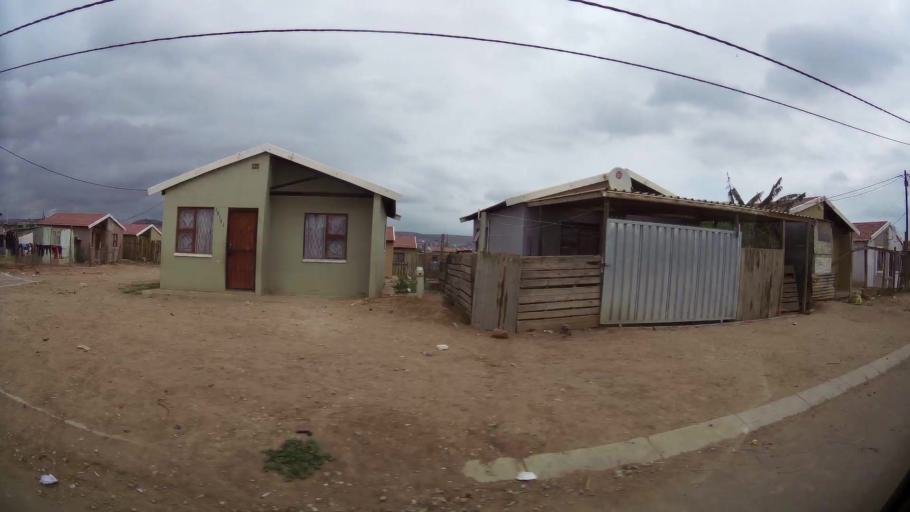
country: ZA
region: Eastern Cape
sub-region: Nelson Mandela Bay Metropolitan Municipality
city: Port Elizabeth
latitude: -33.8832
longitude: 25.5526
